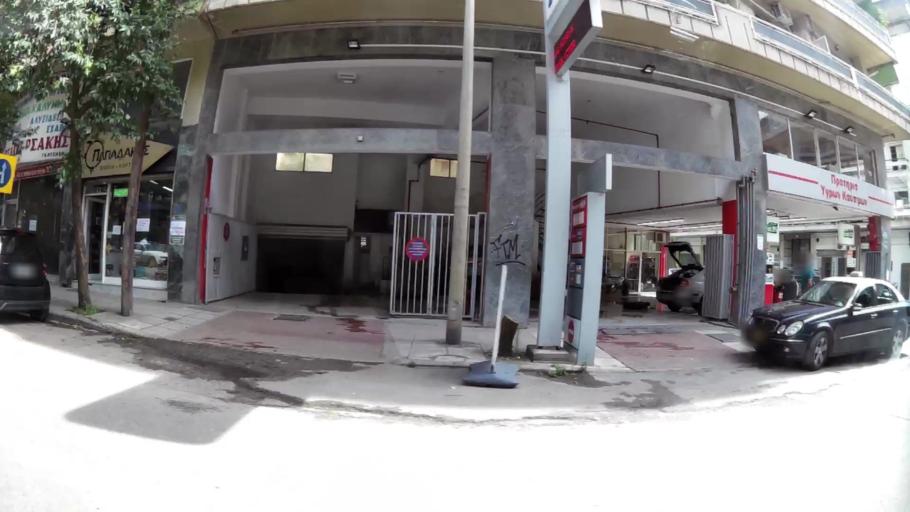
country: GR
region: Central Macedonia
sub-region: Nomos Thessalonikis
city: Triandria
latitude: 40.6044
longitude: 22.9572
